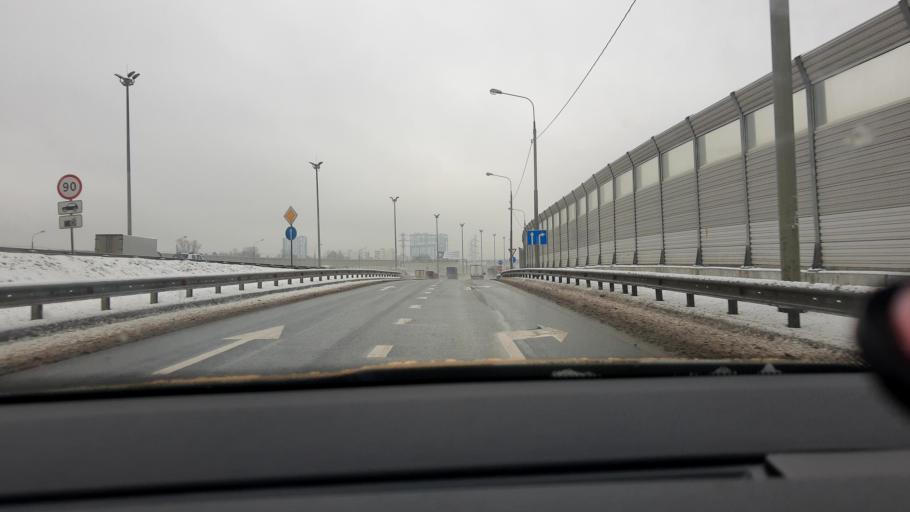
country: RU
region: Moskovskaya
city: Mamontovka
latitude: 55.9637
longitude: 37.8375
